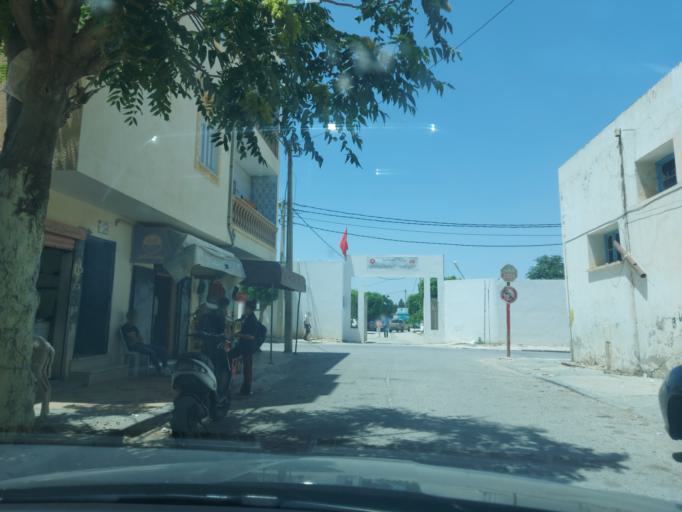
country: TN
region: Silyanah
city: Siliana
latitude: 36.0870
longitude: 9.3681
